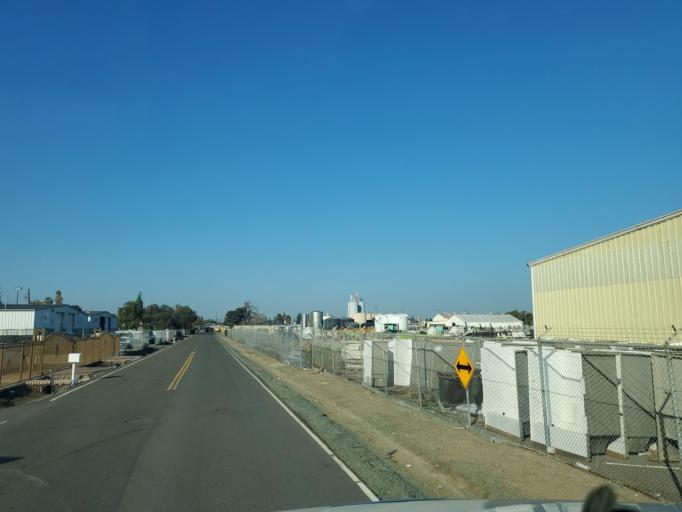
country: US
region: California
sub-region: San Joaquin County
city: August
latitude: 37.9789
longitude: -121.2533
